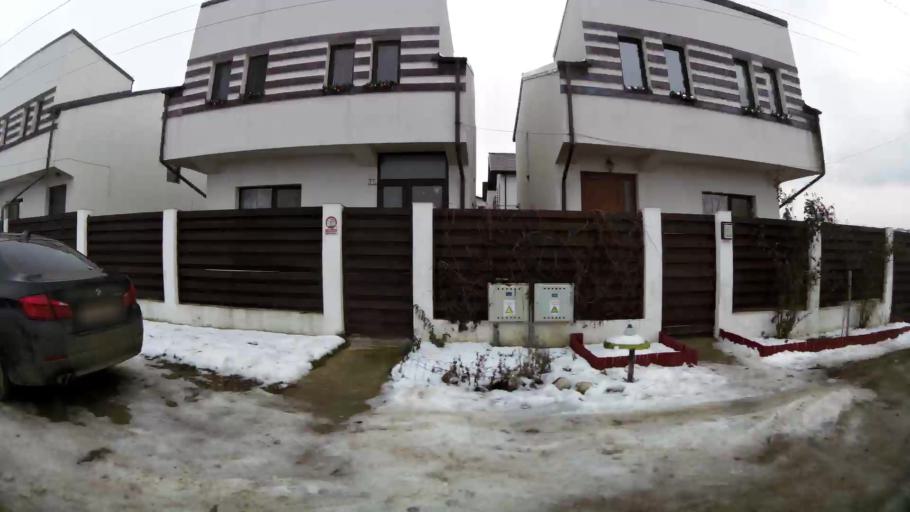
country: RO
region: Ilfov
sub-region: Comuna Tunari
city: Tunari
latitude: 44.5511
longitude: 26.1302
